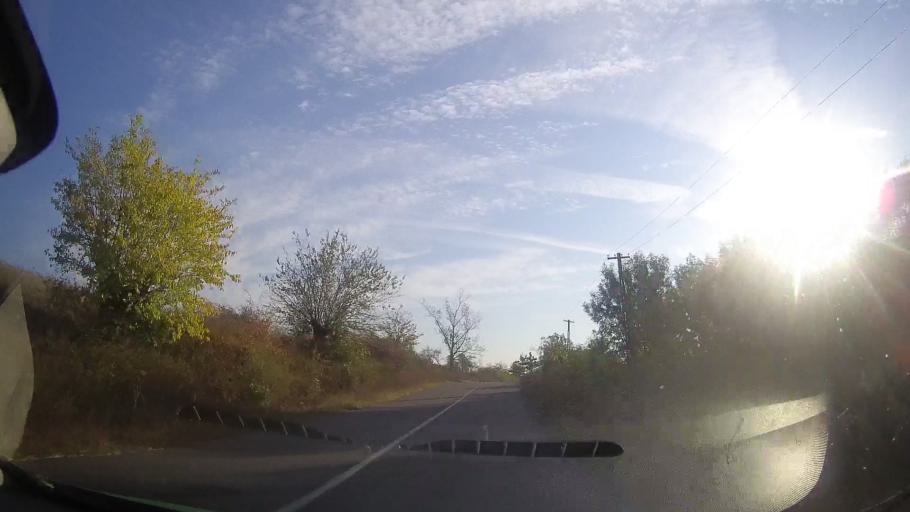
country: RO
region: Timis
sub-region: Comuna Masloc
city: Masloc
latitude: 45.9801
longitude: 21.5083
